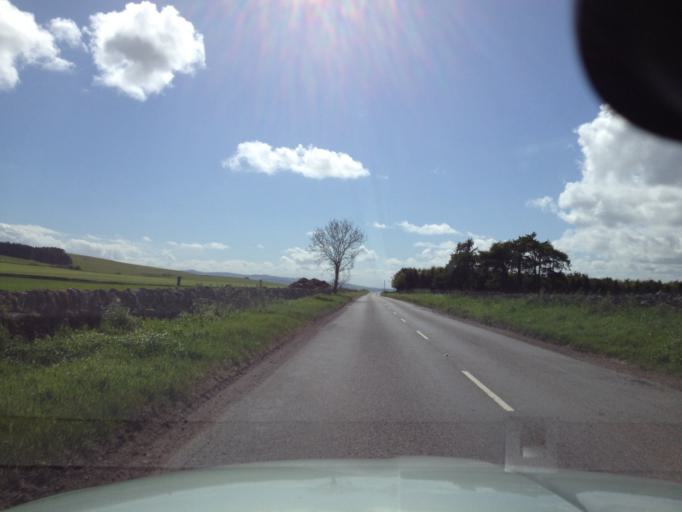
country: GB
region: Scotland
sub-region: Angus
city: Letham
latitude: 56.6801
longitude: -2.8053
